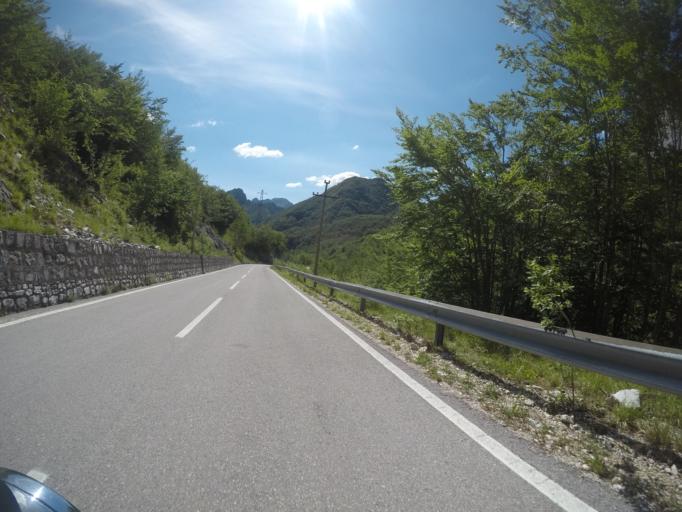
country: IT
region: Tuscany
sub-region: Provincia di Lucca
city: Seravezza
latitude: 44.0603
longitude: 10.2379
